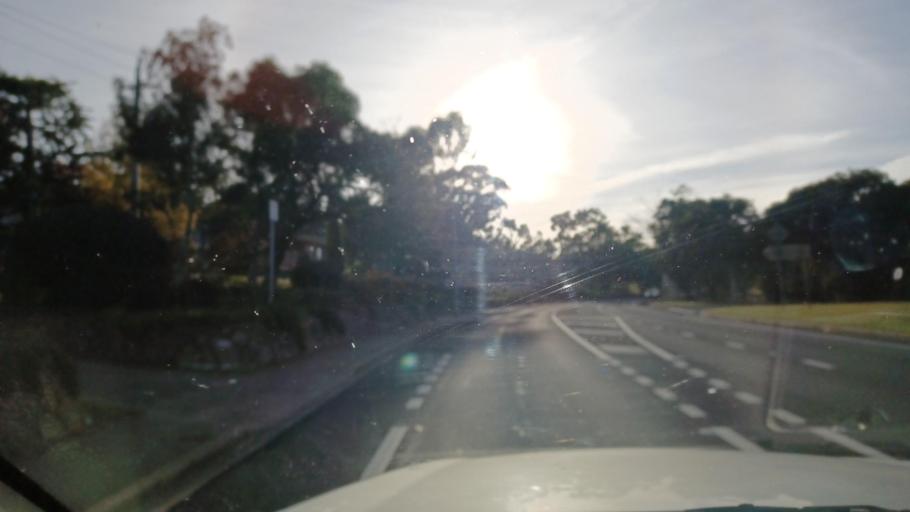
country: AU
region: Australian Capital Territory
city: Belconnen
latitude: -35.2037
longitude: 149.0512
